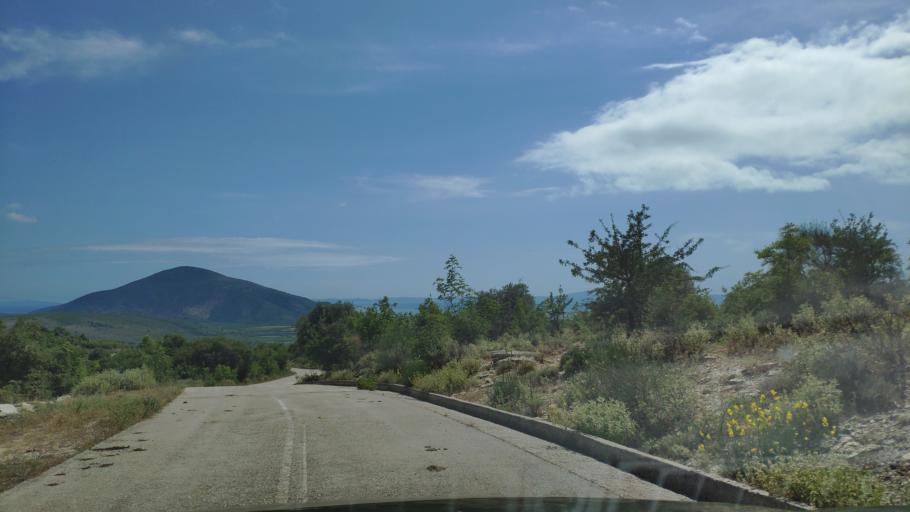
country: AL
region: Vlore
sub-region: Rrethi i Sarandes
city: Konispol
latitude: 39.6305
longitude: 20.2112
